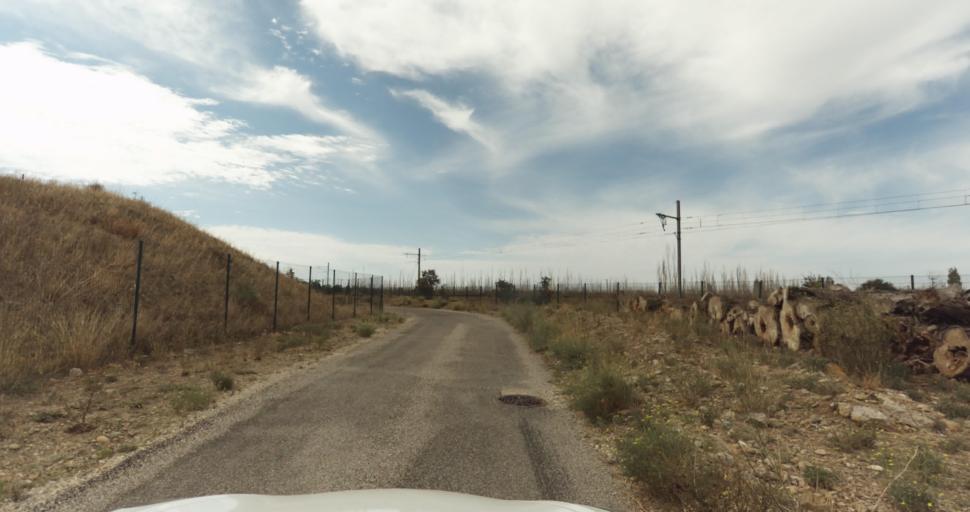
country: FR
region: Provence-Alpes-Cote d'Azur
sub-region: Departement des Bouches-du-Rhone
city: Miramas
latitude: 43.6012
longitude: 4.9891
